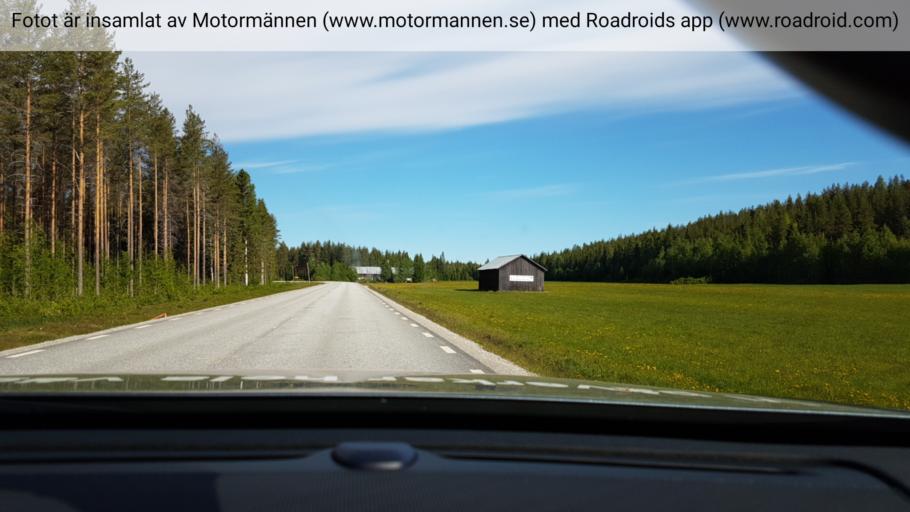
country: SE
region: Vaesterbotten
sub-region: Vindelns Kommun
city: Vindeln
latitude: 64.1990
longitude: 19.4515
